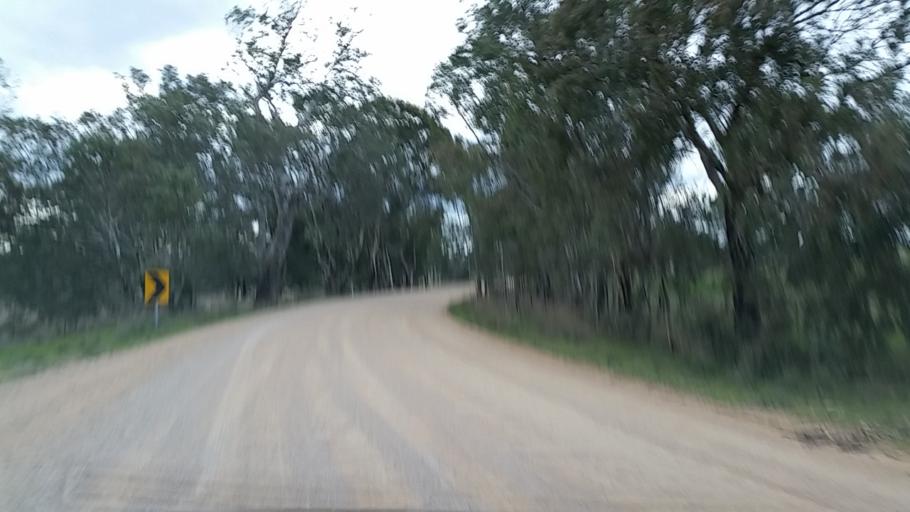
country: AU
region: South Australia
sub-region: Adelaide Hills
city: Birdwood
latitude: -34.8845
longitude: 139.0274
